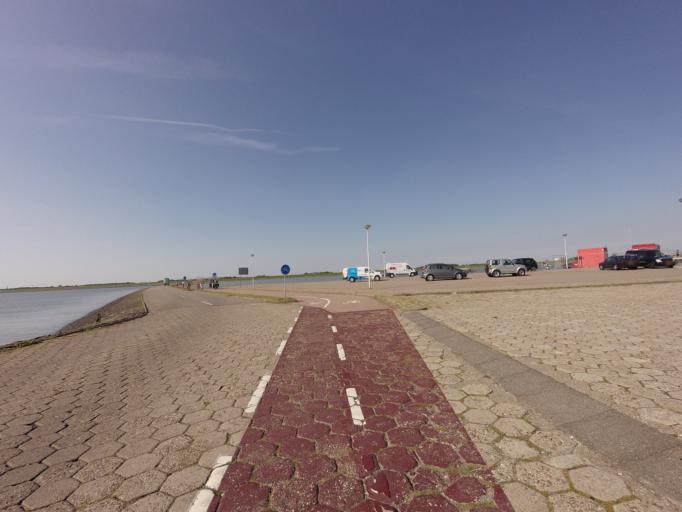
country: NL
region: Friesland
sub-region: Gemeente Schiermonnikoog
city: Schiermonnikoog
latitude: 53.4689
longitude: 6.2009
